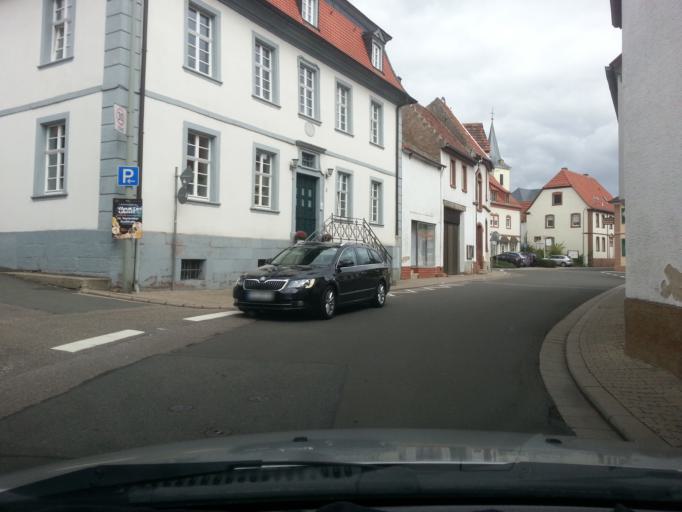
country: DE
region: Rheinland-Pfalz
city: Kerzenheim
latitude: 49.5759
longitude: 8.0605
